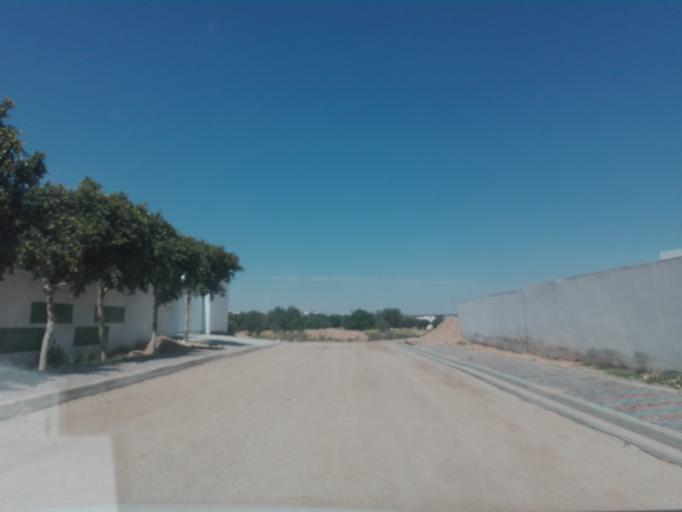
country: TN
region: Safaqis
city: Sfax
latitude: 34.7258
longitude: 10.5125
